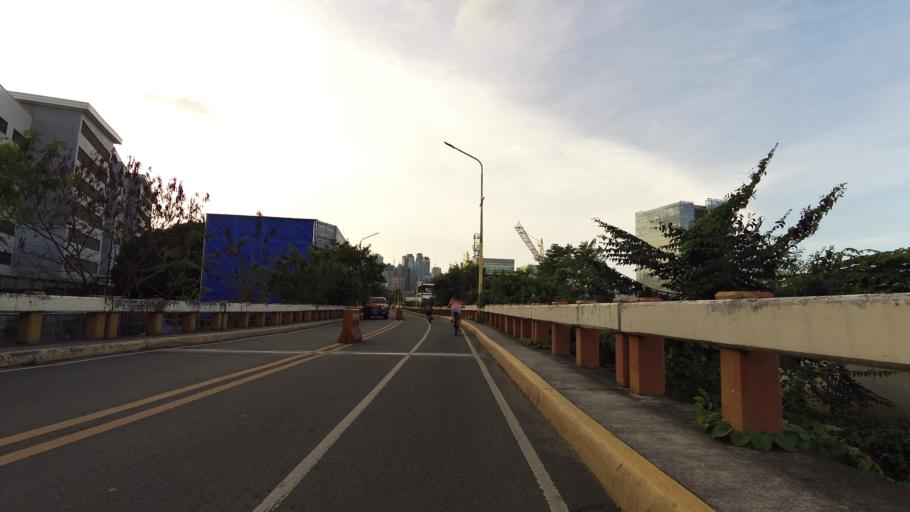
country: PH
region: Metro Manila
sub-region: Pasig
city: Pasig City
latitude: 14.5754
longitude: 121.0758
